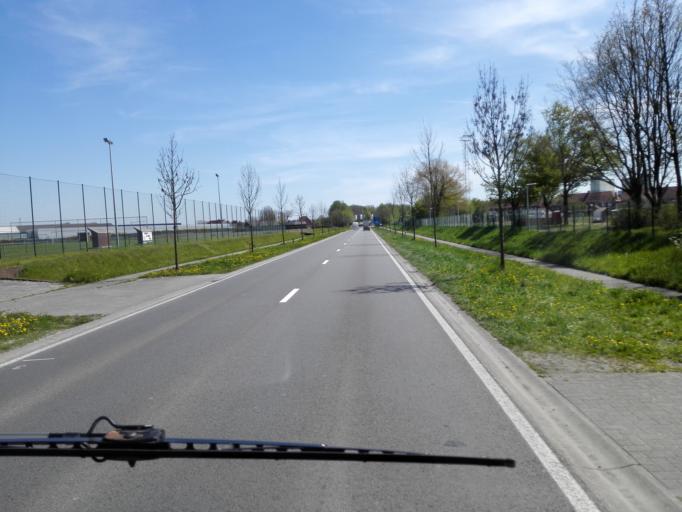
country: BE
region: Flanders
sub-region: Provincie West-Vlaanderen
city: Ingelmunster
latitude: 50.9215
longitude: 3.2647
